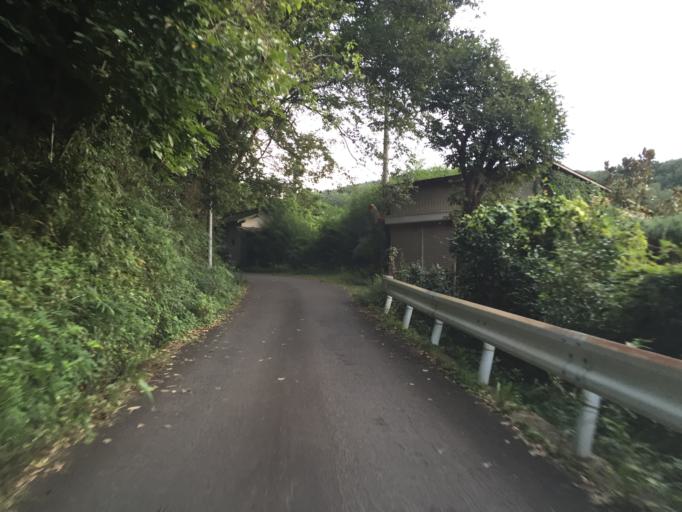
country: JP
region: Fukushima
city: Fukushima-shi
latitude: 37.7654
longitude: 140.4988
